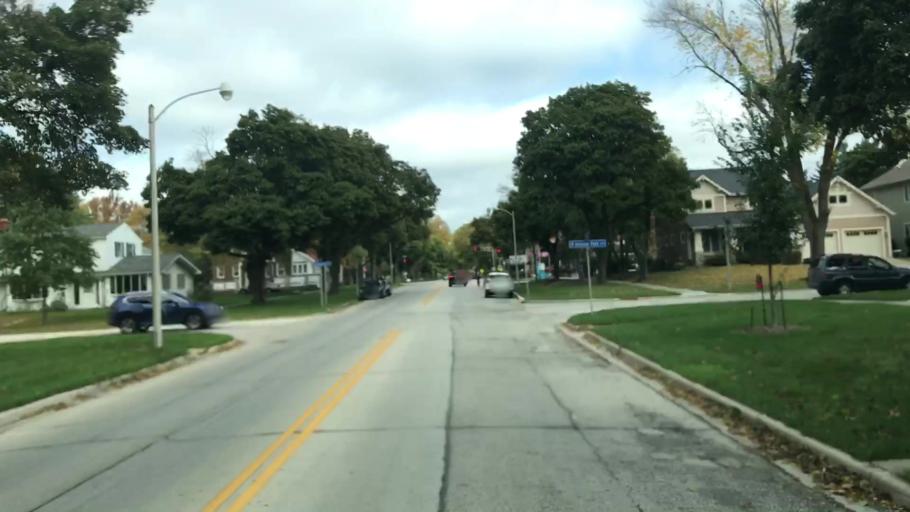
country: US
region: Wisconsin
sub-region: Milwaukee County
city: Wauwatosa
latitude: 43.0591
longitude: -88.0274
